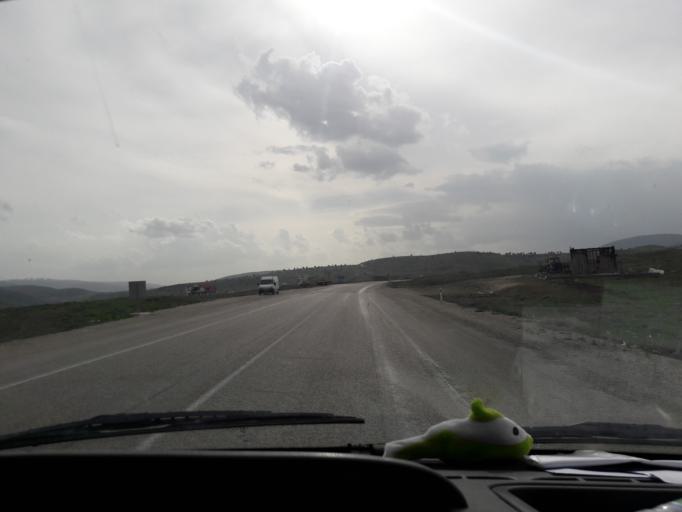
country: TR
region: Gumushane
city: Siran
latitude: 40.1603
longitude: 39.0190
